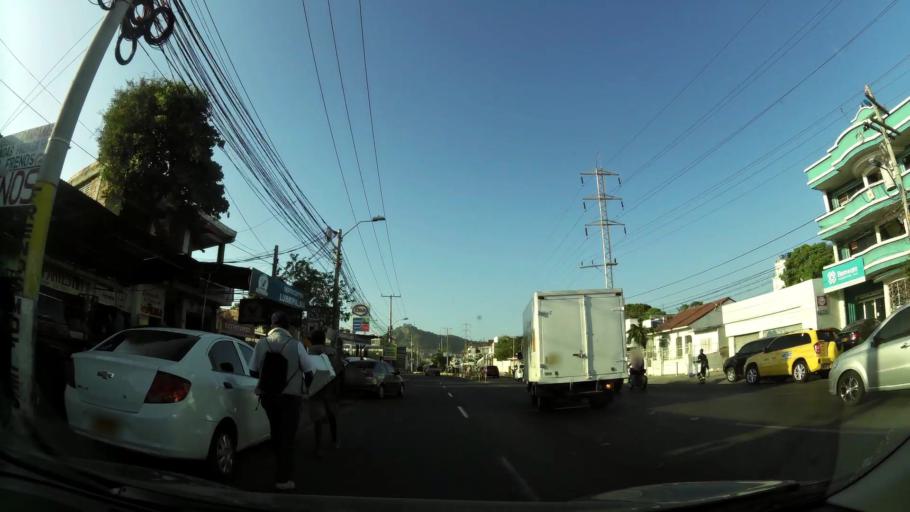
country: CO
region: Bolivar
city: Cartagena
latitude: 10.4043
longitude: -75.5202
